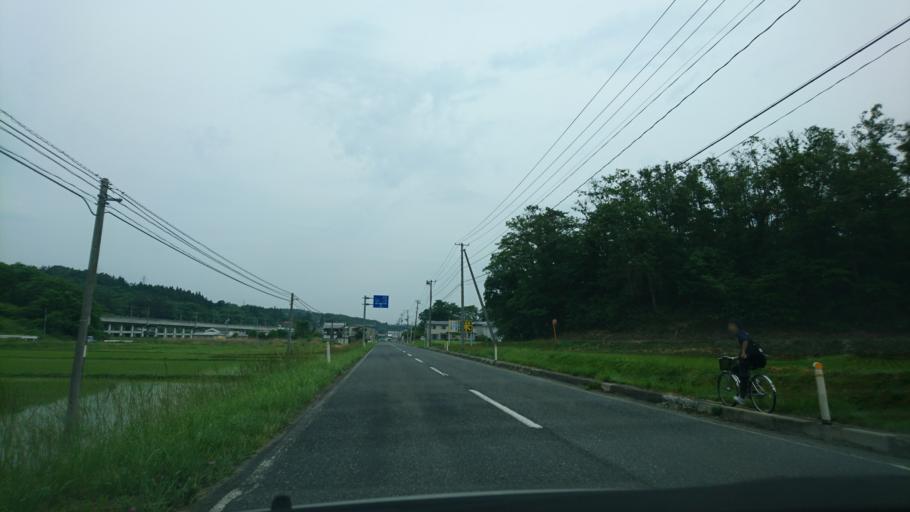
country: JP
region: Iwate
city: Ichinoseki
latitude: 38.8958
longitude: 141.1313
